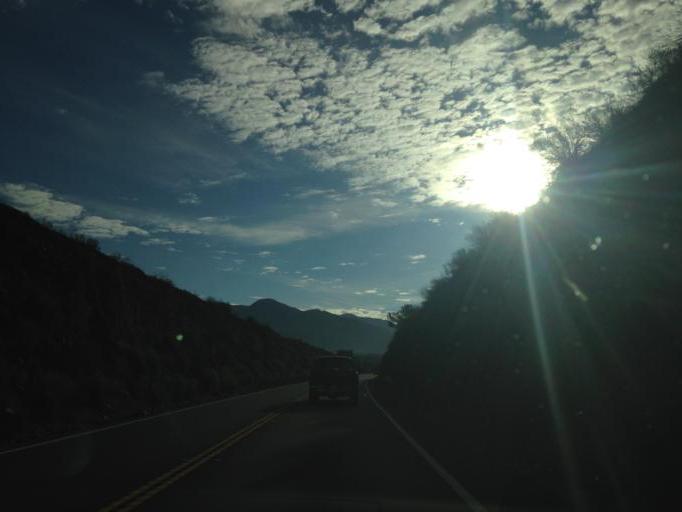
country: US
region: California
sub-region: San Diego County
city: Rainbow
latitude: 33.3632
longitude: -117.0523
